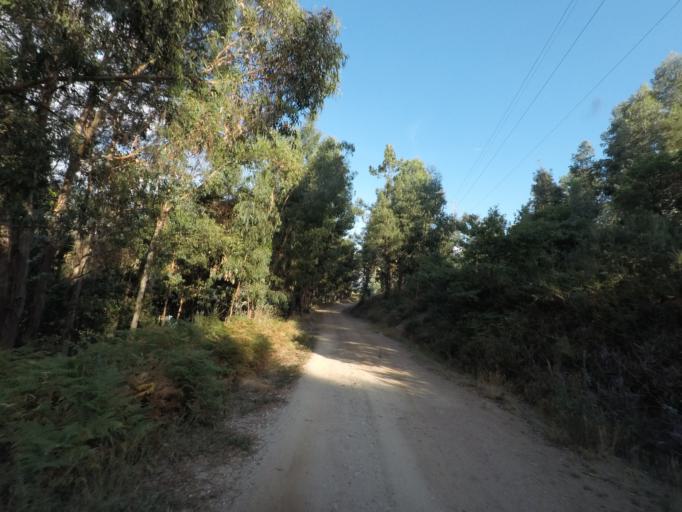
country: PT
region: Vila Real
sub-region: Mesao Frio
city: Mesao Frio
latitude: 41.1706
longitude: -7.9050
